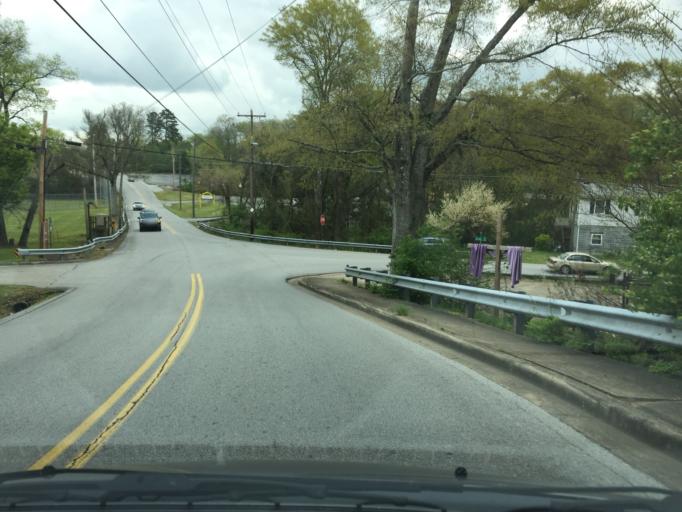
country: US
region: Tennessee
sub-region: Hamilton County
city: Falling Water
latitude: 35.1431
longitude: -85.2389
